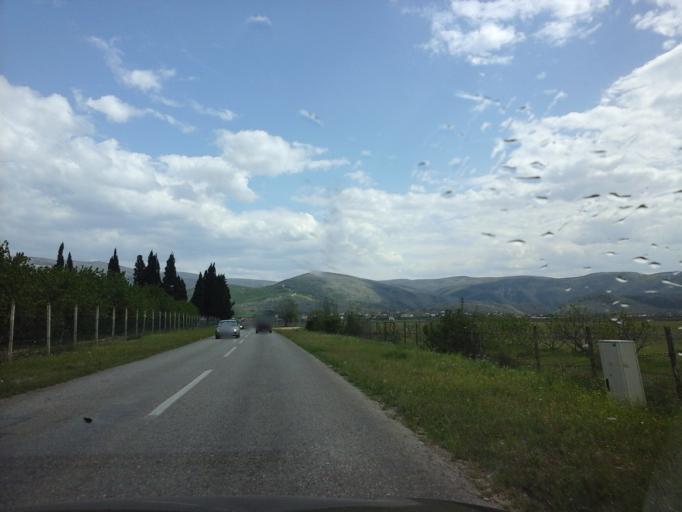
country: BA
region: Federation of Bosnia and Herzegovina
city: Blagaj
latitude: 43.2715
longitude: 17.8598
